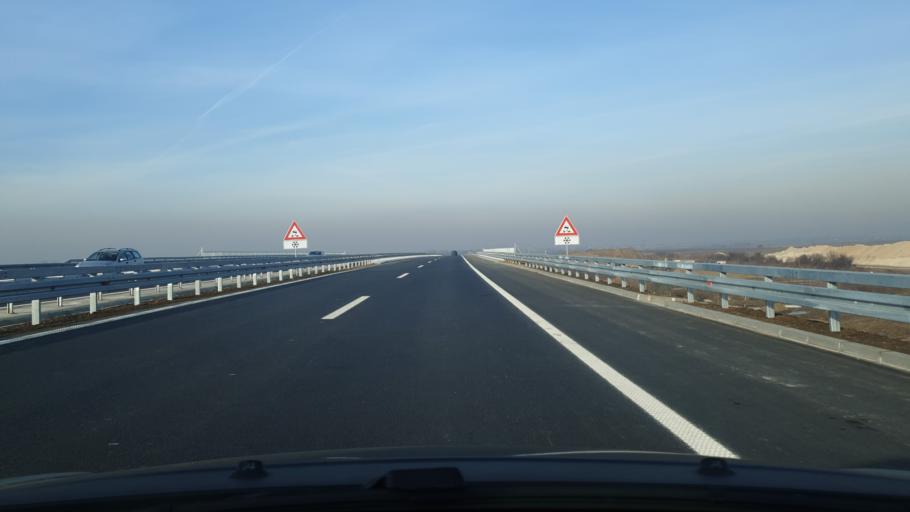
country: RS
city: Boljevci
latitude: 44.7158
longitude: 20.2586
